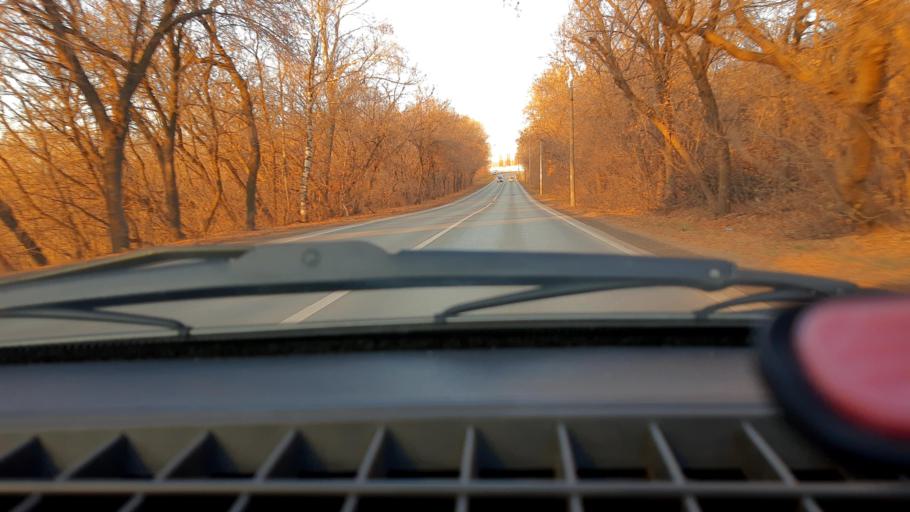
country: RU
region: Bashkortostan
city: Ufa
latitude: 54.8565
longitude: 56.0742
